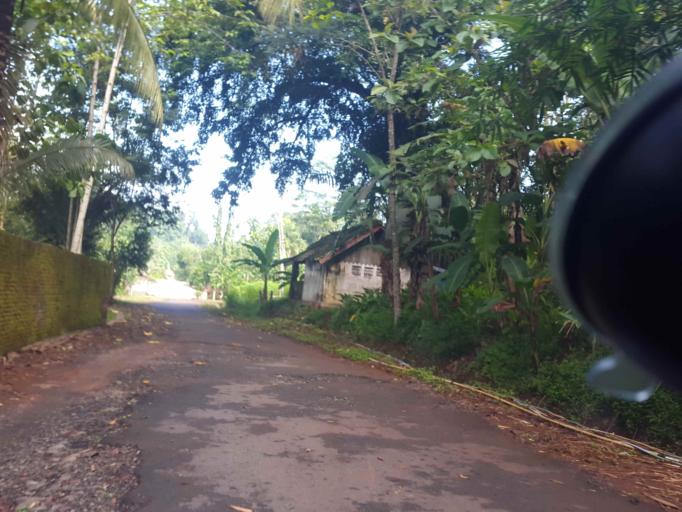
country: ID
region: Central Java
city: Gambarsari
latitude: -7.5239
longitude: 109.1989
